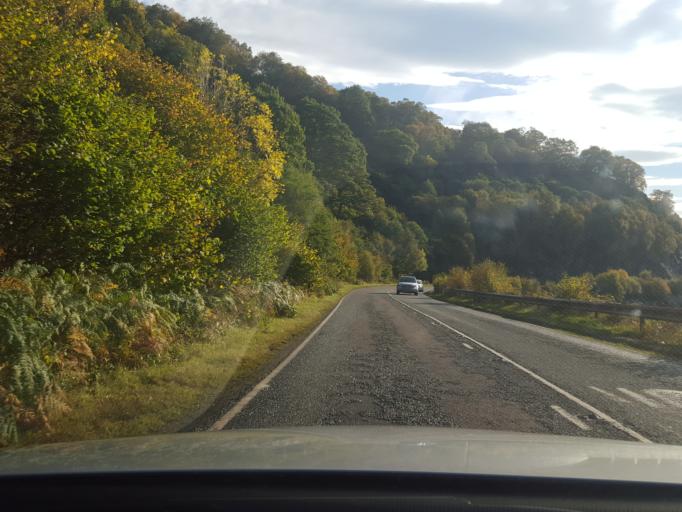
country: GB
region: Scotland
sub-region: Highland
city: Fort William
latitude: 57.2677
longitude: -5.5059
